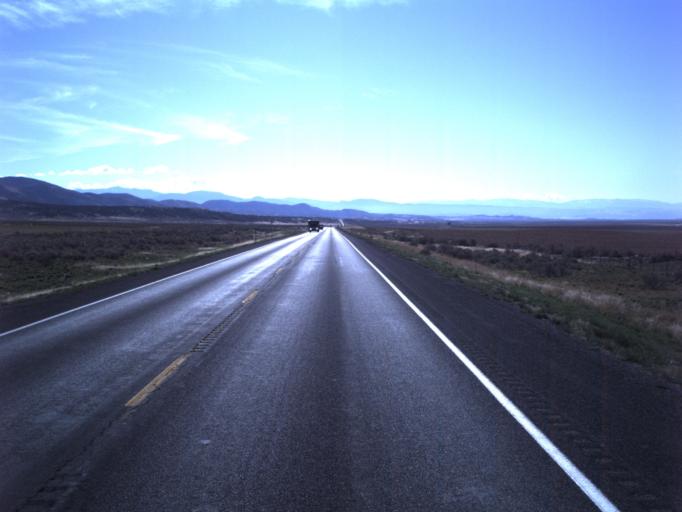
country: US
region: Utah
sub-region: Sanpete County
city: Gunnison
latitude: 39.3194
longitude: -111.9065
